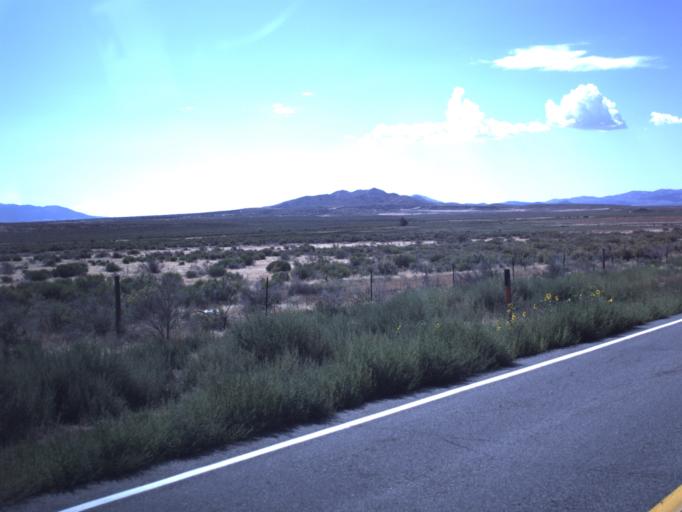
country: US
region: Utah
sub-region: Tooele County
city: Tooele
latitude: 40.2010
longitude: -112.4120
